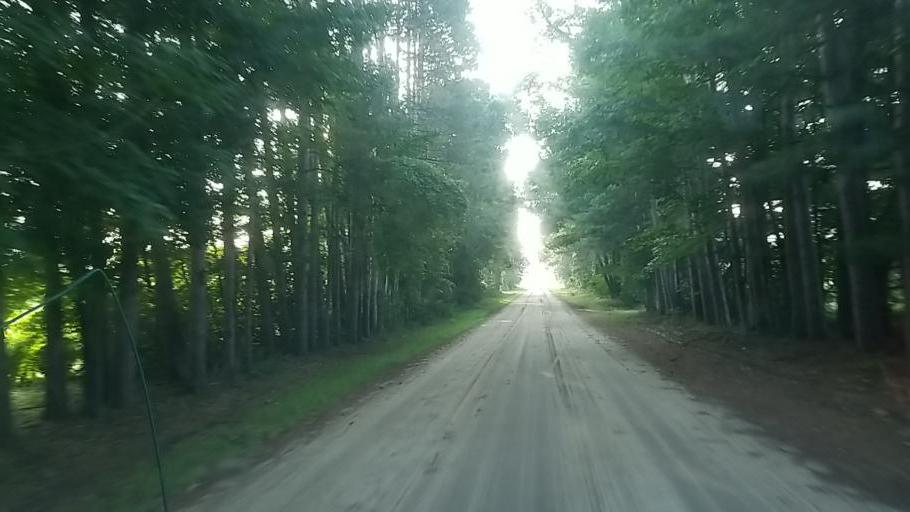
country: US
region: Michigan
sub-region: Muskegon County
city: Twin Lake
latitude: 43.4533
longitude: -86.0877
